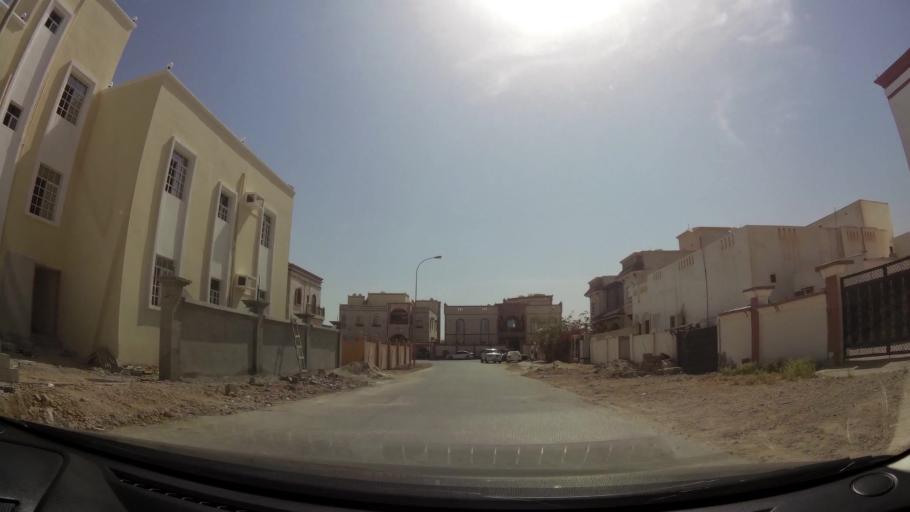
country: OM
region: Zufar
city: Salalah
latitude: 17.0498
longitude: 54.1507
